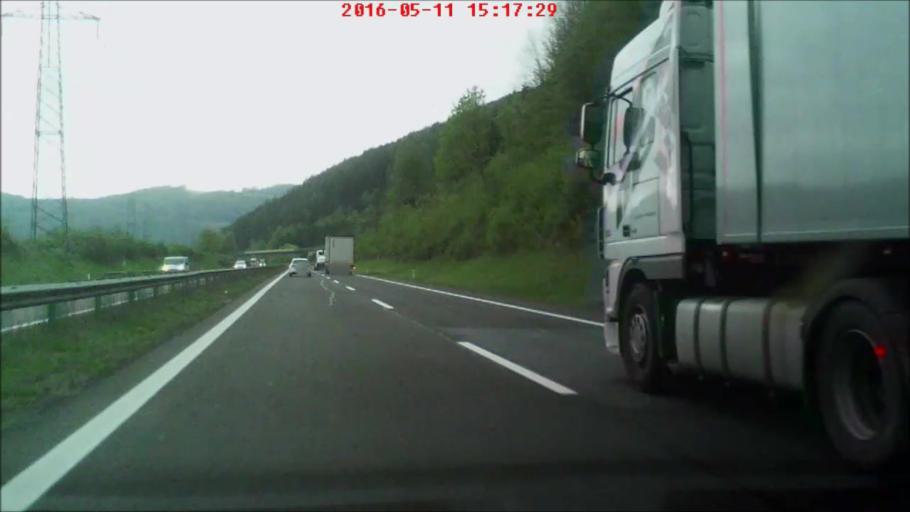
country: AT
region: Styria
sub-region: Politischer Bezirk Leoben
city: Traboch
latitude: 47.3760
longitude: 14.9565
